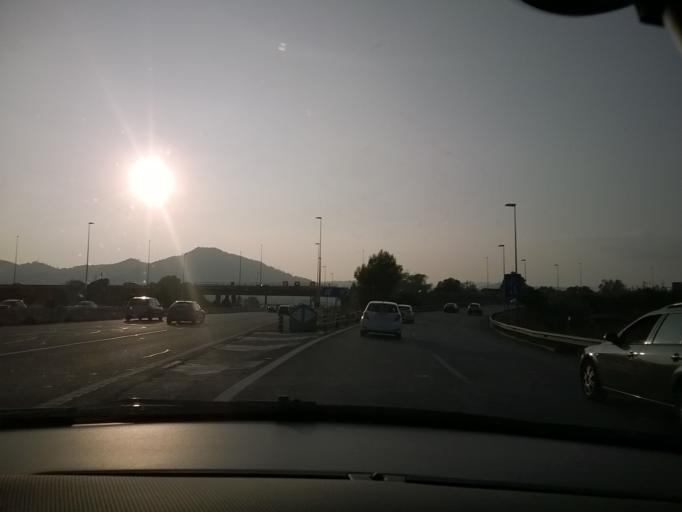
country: ES
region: Catalonia
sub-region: Provincia de Barcelona
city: Sant Feliu de Llobregat
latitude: 41.3733
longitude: 2.0401
